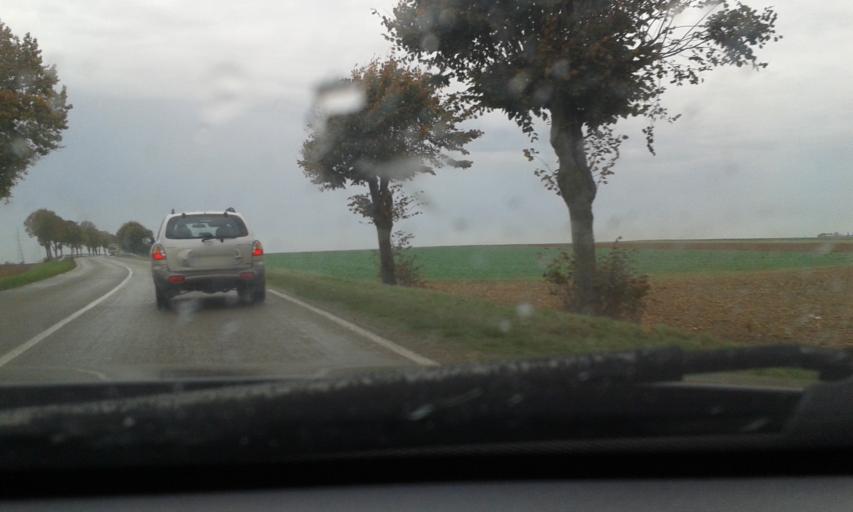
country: FR
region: Centre
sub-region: Departement d'Eure-et-Loir
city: Baigneaux
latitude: 48.1643
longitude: 1.8400
